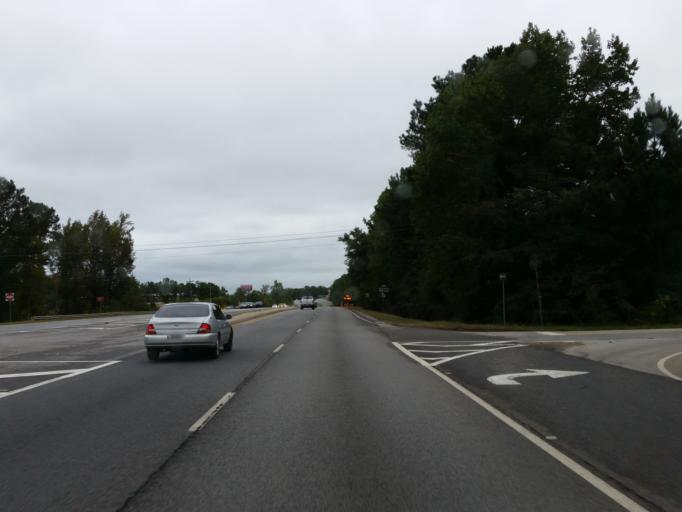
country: US
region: Georgia
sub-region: Clayton County
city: Lovejoy
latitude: 33.4035
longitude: -84.3127
